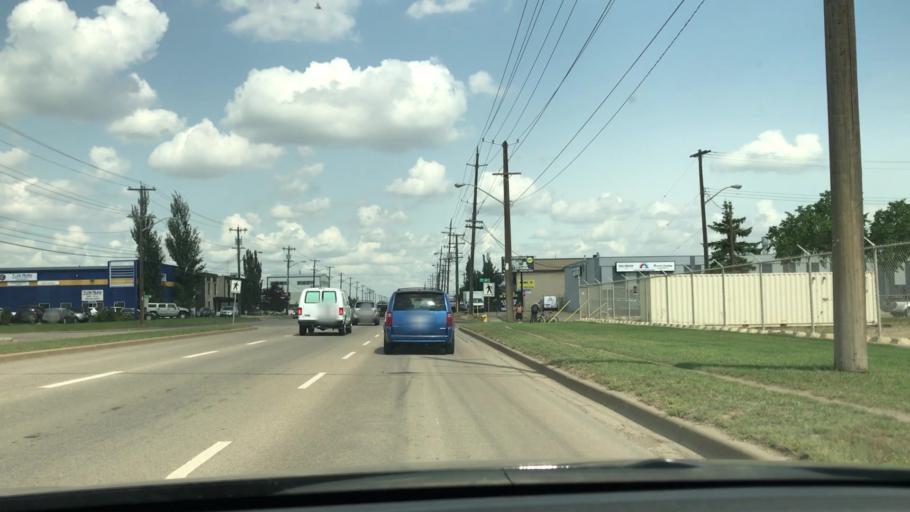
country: CA
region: Alberta
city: Edmonton
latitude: 53.5076
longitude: -113.4182
